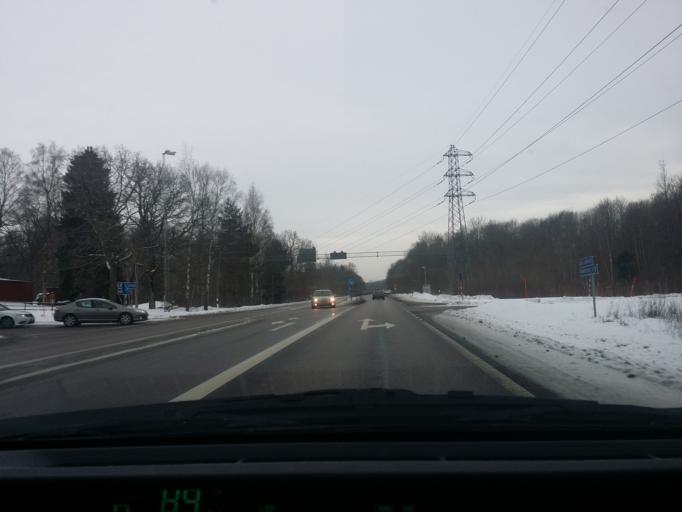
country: SE
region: Vaestra Goetaland
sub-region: Skovde Kommun
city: Stopen
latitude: 58.4758
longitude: 13.8507
